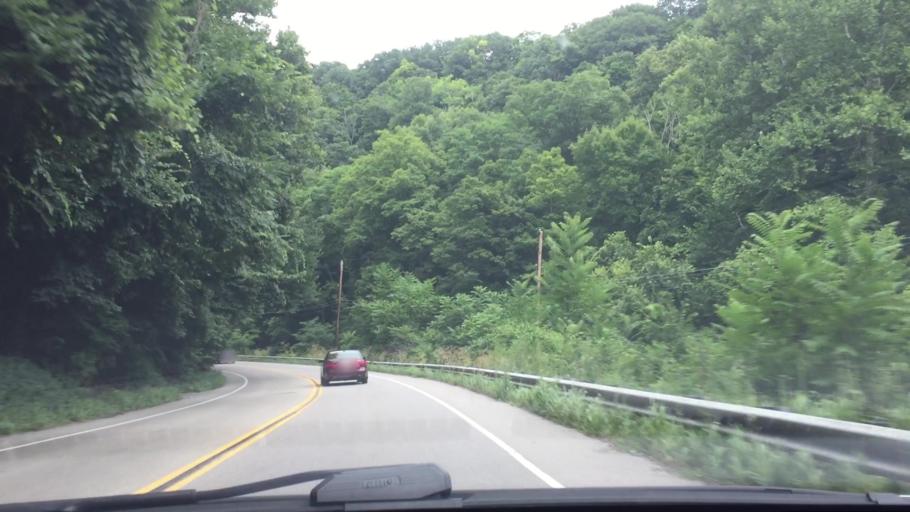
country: US
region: Pennsylvania
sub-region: Allegheny County
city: Bridgeville
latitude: 40.3616
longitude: -80.0889
